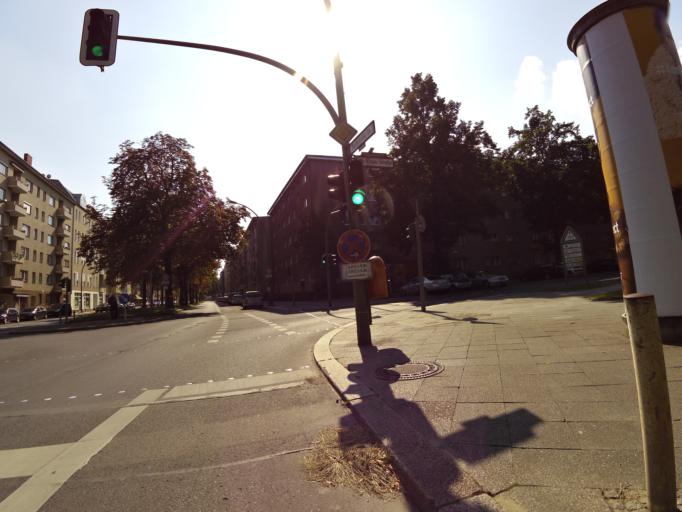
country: DE
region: Berlin
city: Berlin Schoeneberg
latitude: 52.4828
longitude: 13.3450
